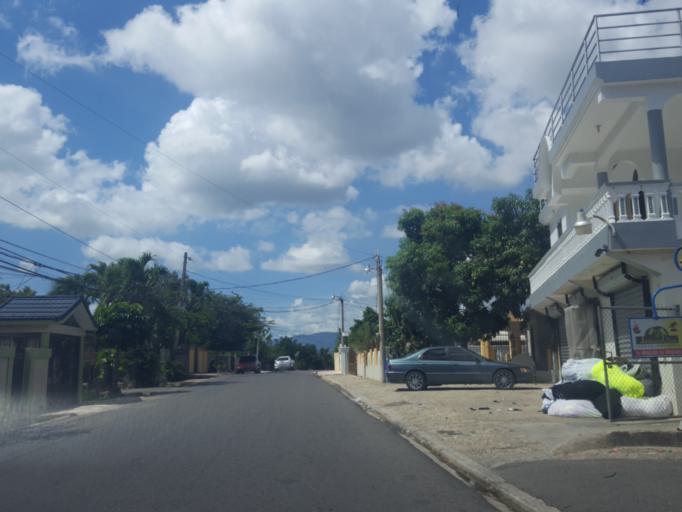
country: DO
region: Santiago
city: Licey al Medio
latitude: 19.3917
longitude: -70.6485
